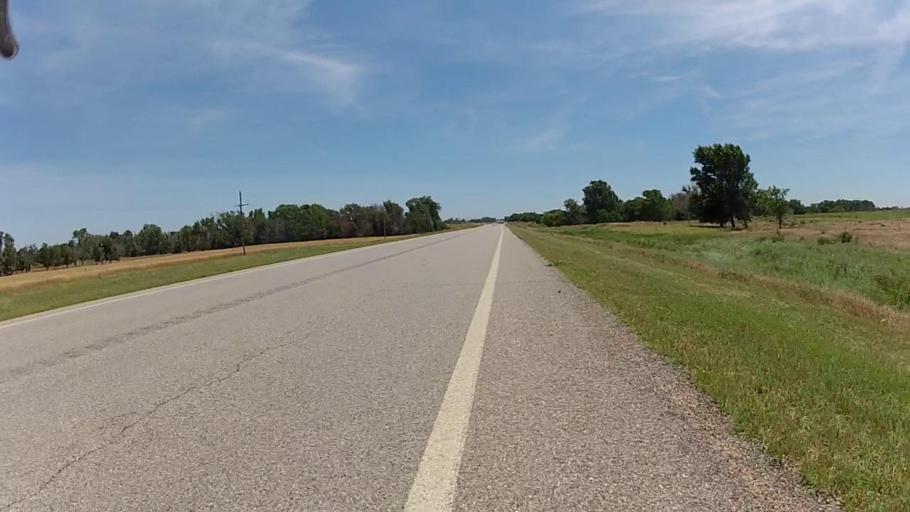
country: US
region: Kansas
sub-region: Barber County
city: Medicine Lodge
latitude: 37.2535
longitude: -98.4756
